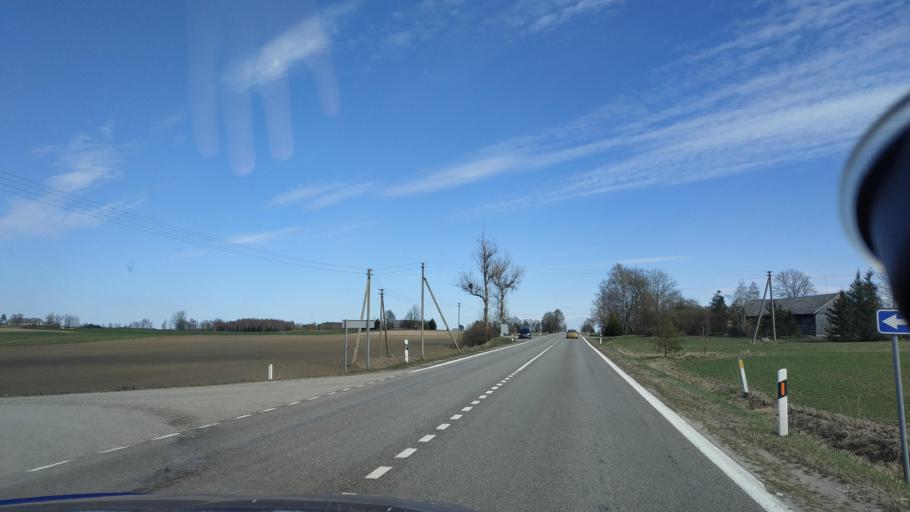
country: LT
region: Marijampoles apskritis
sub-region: Marijampole Municipality
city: Marijampole
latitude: 54.5481
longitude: 23.4669
